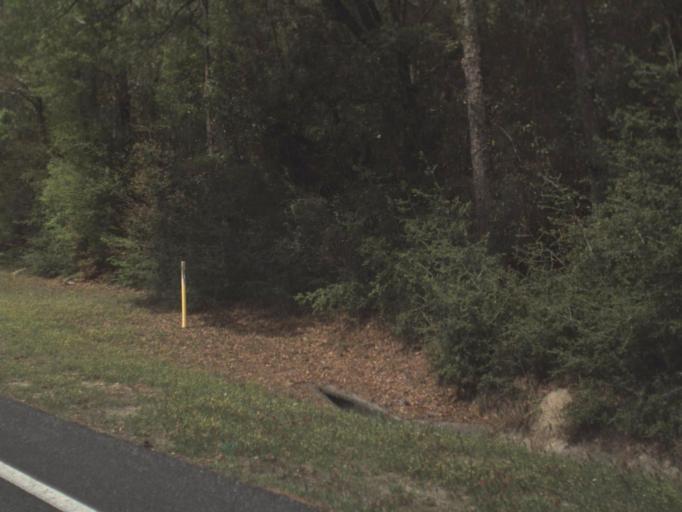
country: US
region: Florida
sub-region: Okaloosa County
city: Crestview
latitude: 30.7573
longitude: -86.6117
